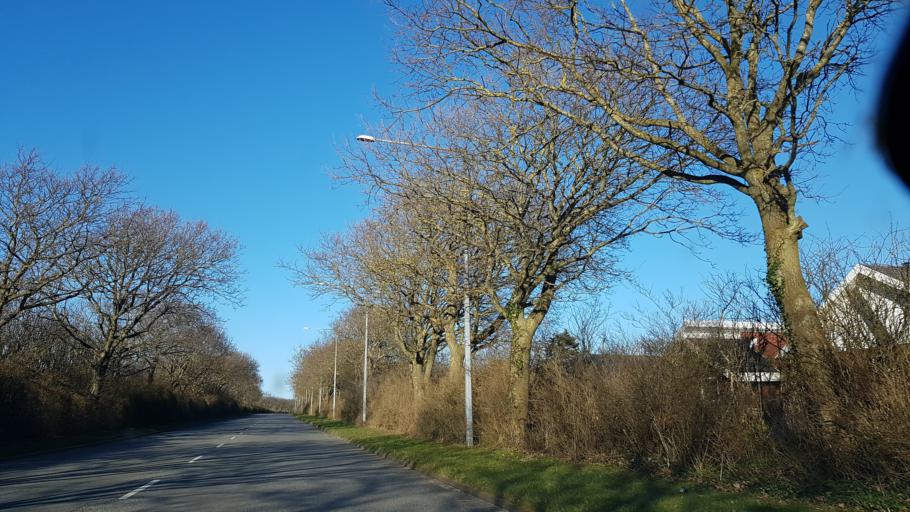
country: DK
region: South Denmark
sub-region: Fano Kommune
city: Nordby
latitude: 55.5086
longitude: 8.3875
